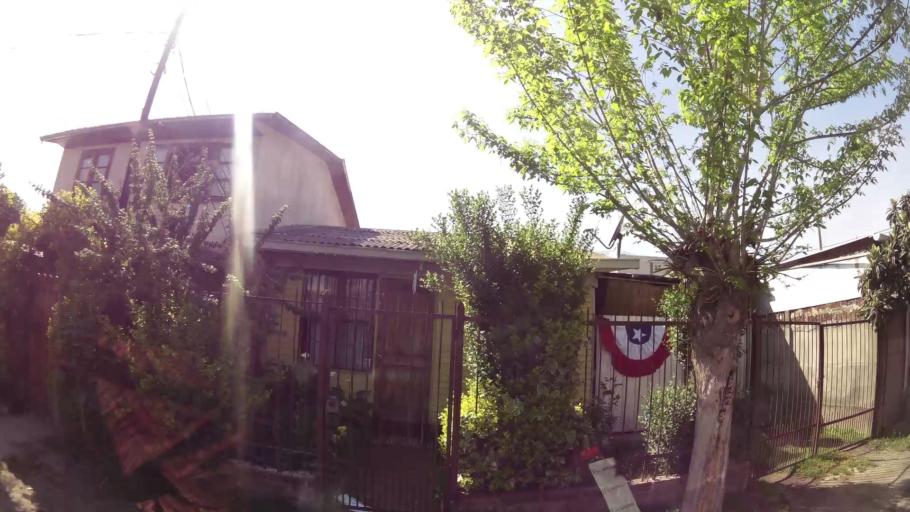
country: CL
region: Santiago Metropolitan
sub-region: Provincia de Santiago
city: Villa Presidente Frei, Nunoa, Santiago, Chile
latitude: -33.5260
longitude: -70.5586
